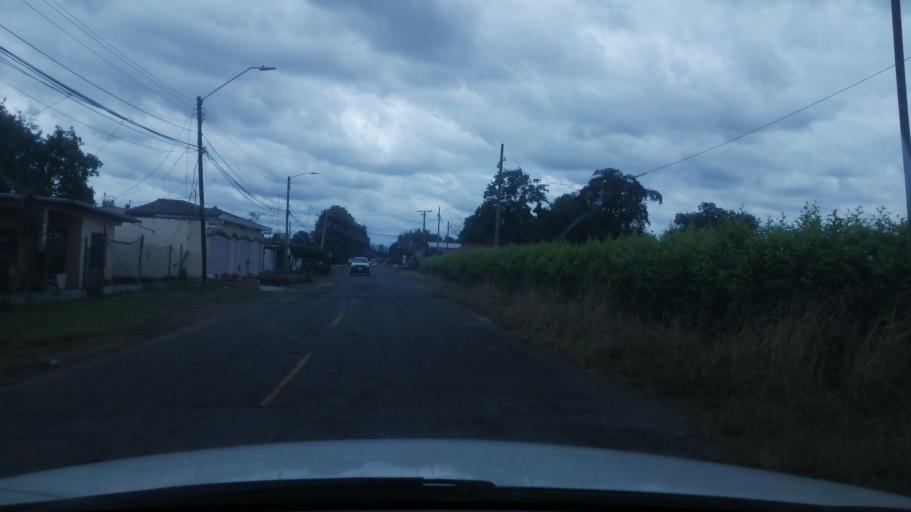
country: PA
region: Chiriqui
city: David
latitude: 8.4207
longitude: -82.4355
